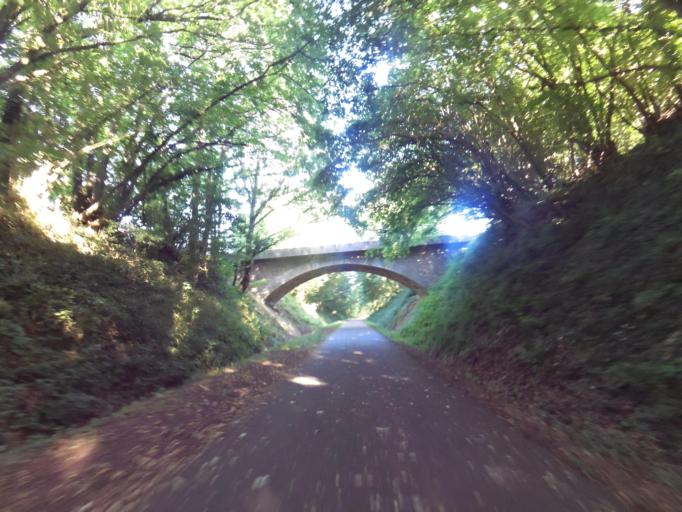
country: FR
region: Brittany
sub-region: Departement du Morbihan
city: Malestroit
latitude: 47.8152
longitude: -2.4107
